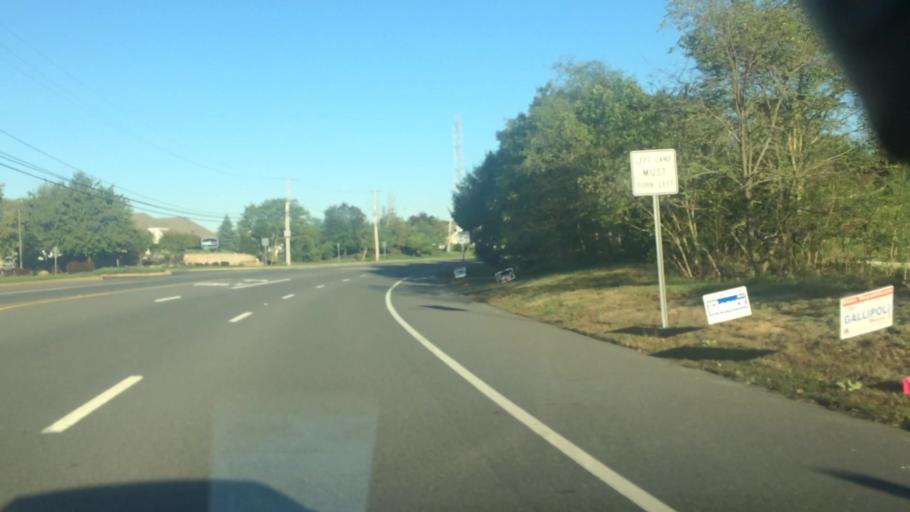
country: US
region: New Jersey
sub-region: Ocean County
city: Silver Ridge
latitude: 39.9870
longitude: -74.2004
